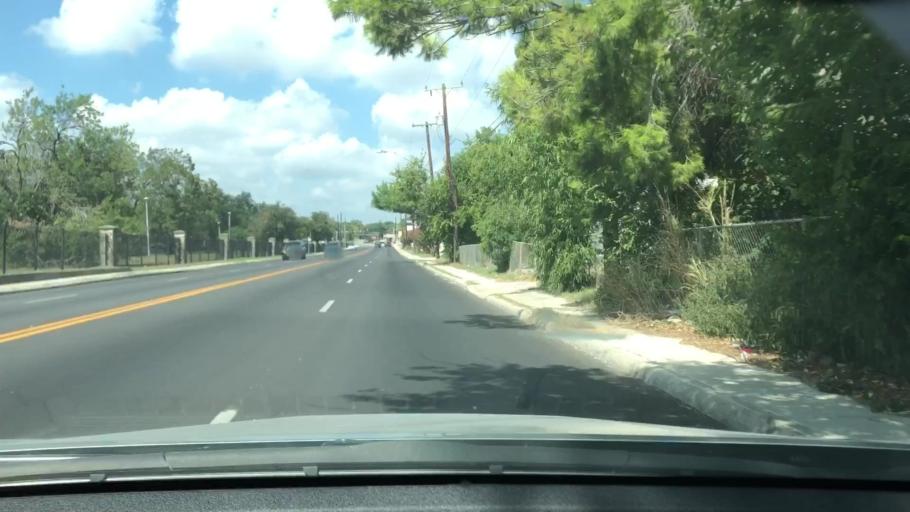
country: US
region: Texas
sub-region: Bexar County
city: Terrell Hills
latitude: 29.4849
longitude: -98.4258
